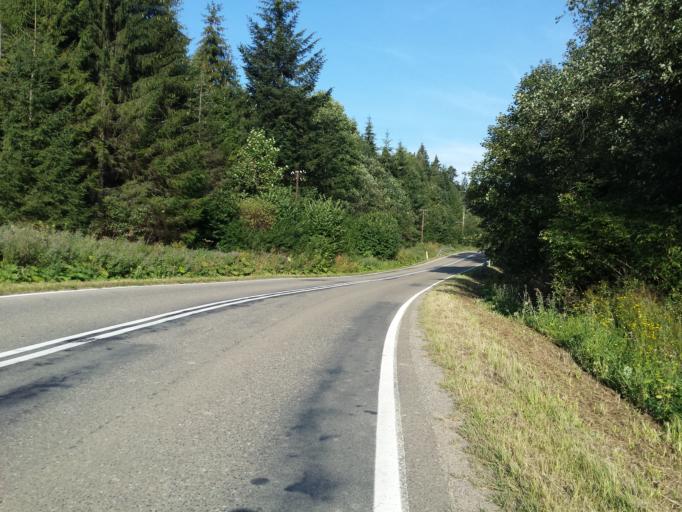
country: PL
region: Subcarpathian Voivodeship
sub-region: Powiat leski
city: Cisna
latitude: 49.2250
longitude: 22.3066
